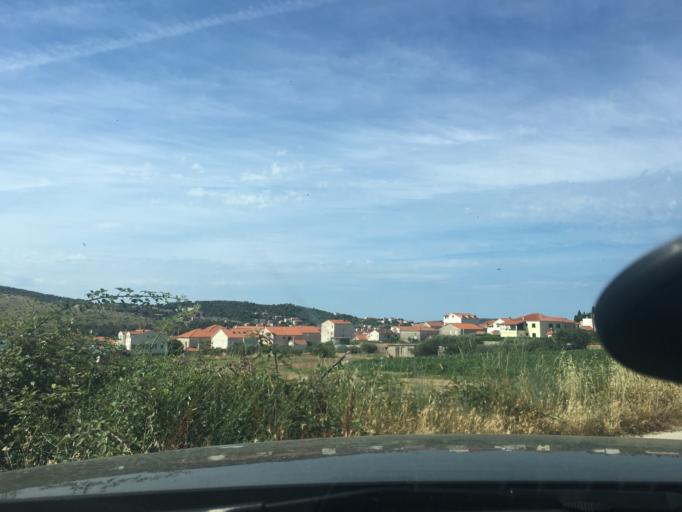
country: HR
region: Splitsko-Dalmatinska
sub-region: Grad Trogir
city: Trogir
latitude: 43.5268
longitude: 16.2630
